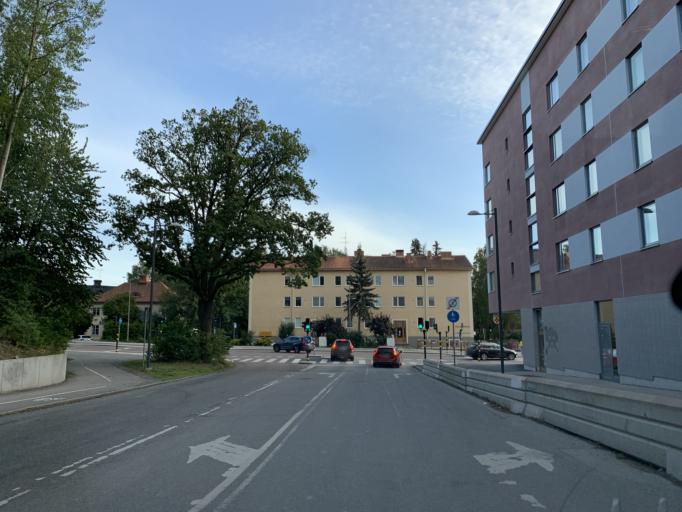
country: SE
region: Stockholm
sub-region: Sundbybergs Kommun
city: Sundbyberg
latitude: 59.3613
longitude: 17.9502
